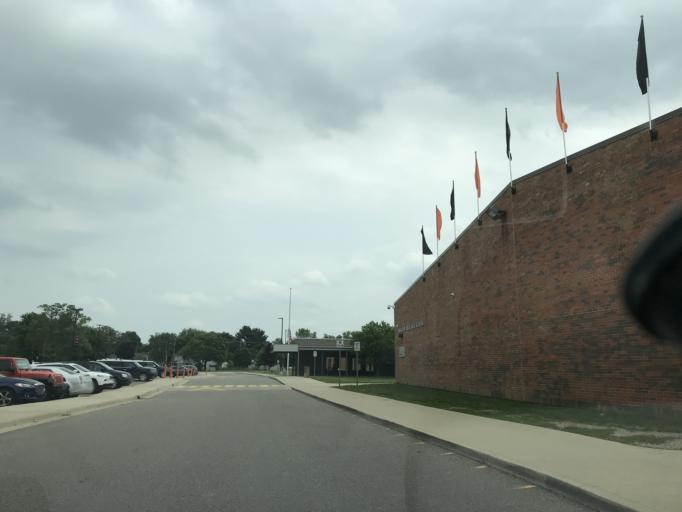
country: US
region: Michigan
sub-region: Livingston County
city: Brighton
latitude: 42.5269
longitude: -83.7946
